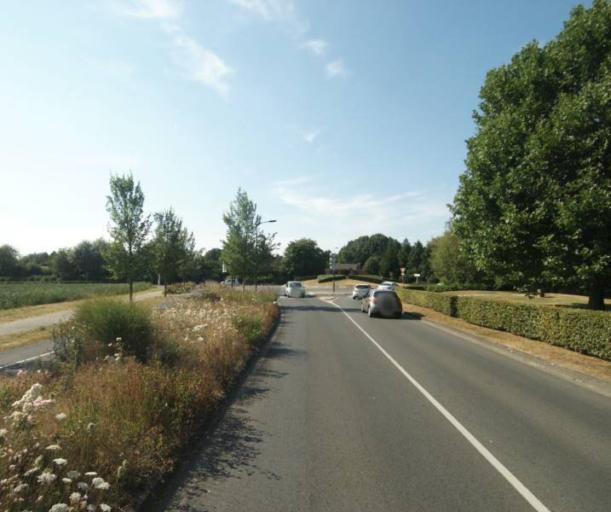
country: FR
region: Nord-Pas-de-Calais
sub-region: Departement du Nord
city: Bondues
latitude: 50.7032
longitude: 3.0838
